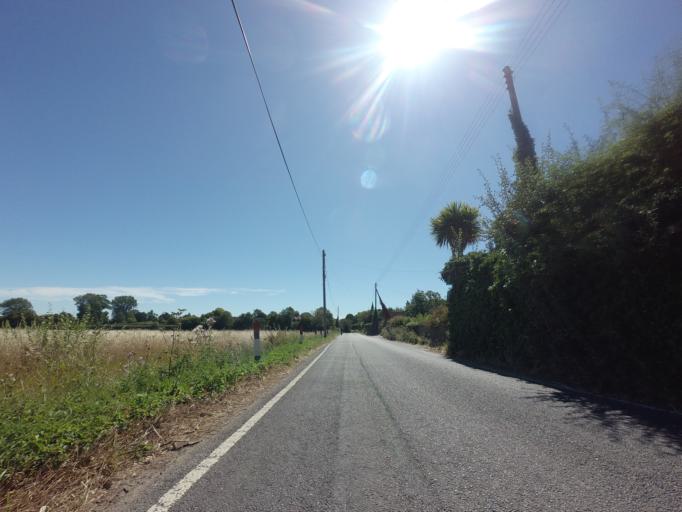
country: GB
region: England
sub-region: Kent
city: Ash
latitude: 51.2701
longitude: 1.2994
